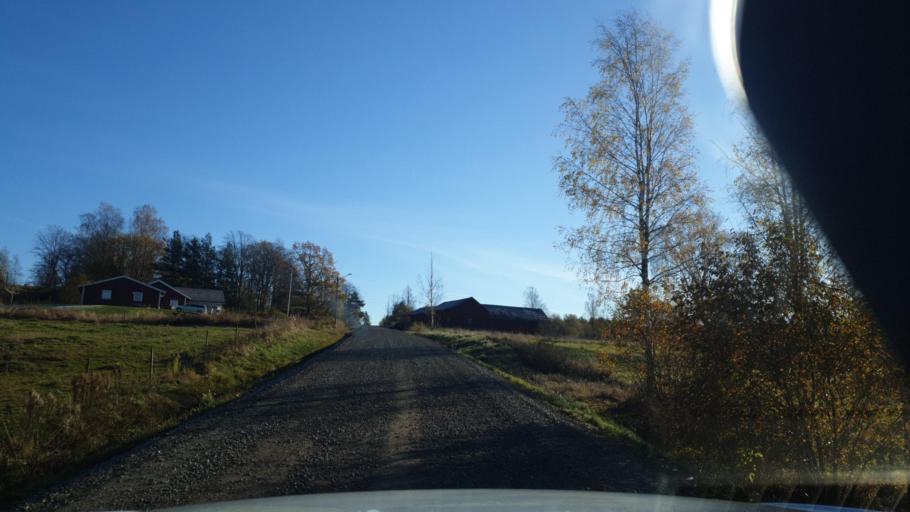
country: SE
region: Vaermland
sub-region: Karlstads Kommun
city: Valberg
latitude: 59.4205
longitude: 13.1063
